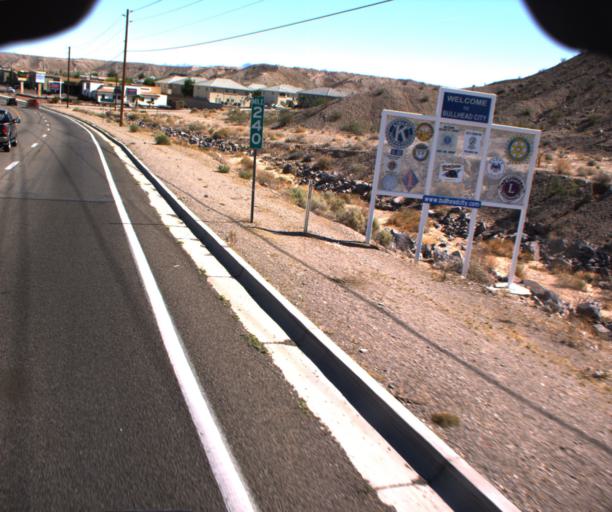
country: US
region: Arizona
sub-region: Mohave County
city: Bullhead City
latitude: 35.0464
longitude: -114.5893
